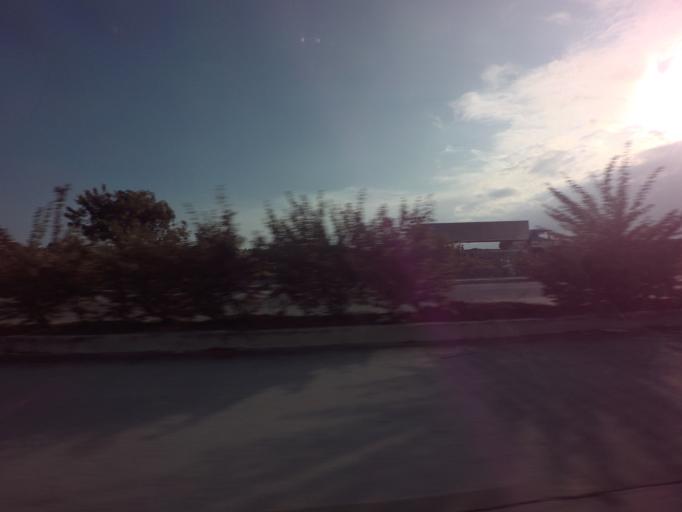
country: PH
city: Sambayanihan People's Village
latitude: 14.5024
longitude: 121.0136
